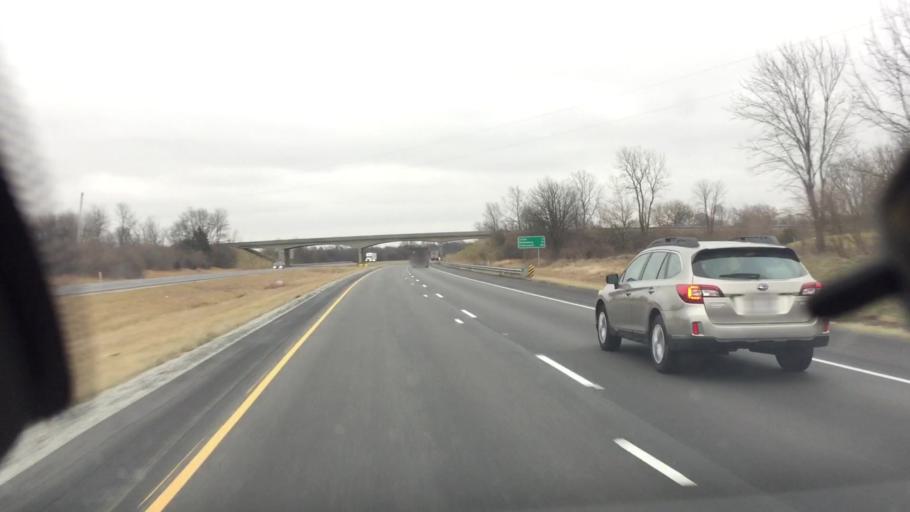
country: US
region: Indiana
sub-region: Hendricks County
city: Pittsboro
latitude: 39.9375
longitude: -86.6072
